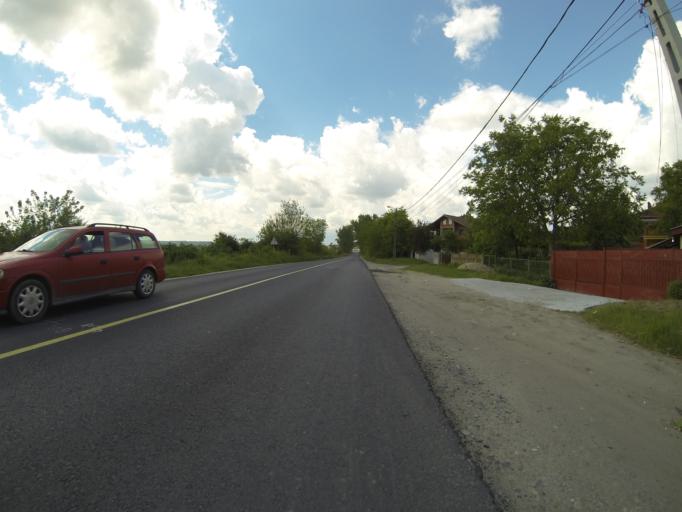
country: RO
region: Dolj
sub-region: Municipiul Craiova
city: Facai
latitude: 44.2685
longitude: 23.8240
